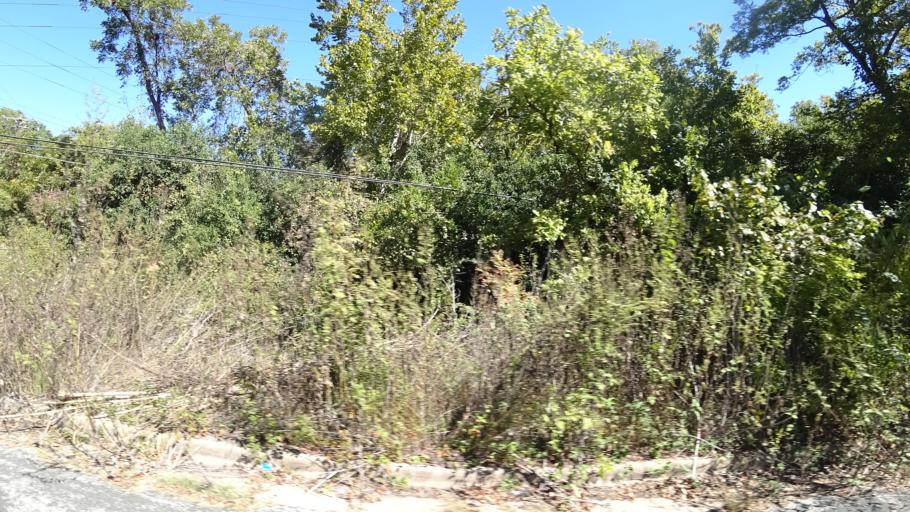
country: US
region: Texas
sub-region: Travis County
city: Austin
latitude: 30.2957
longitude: -97.7125
